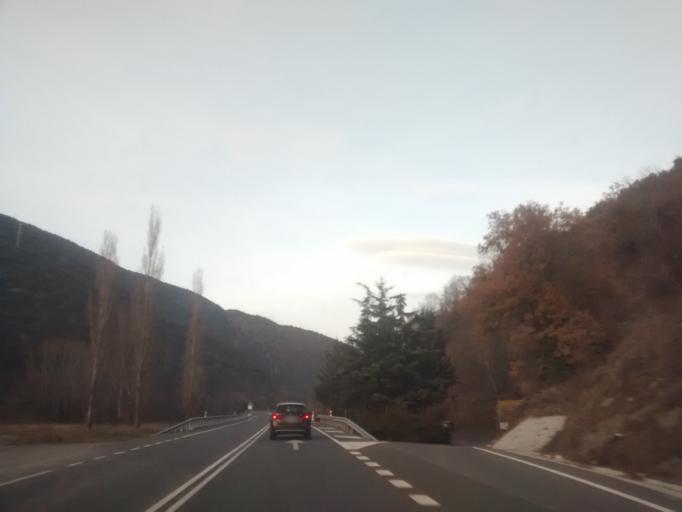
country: ES
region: Catalonia
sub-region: Provincia de Lleida
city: la Seu d'Urgell
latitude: 42.3841
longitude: 1.4599
